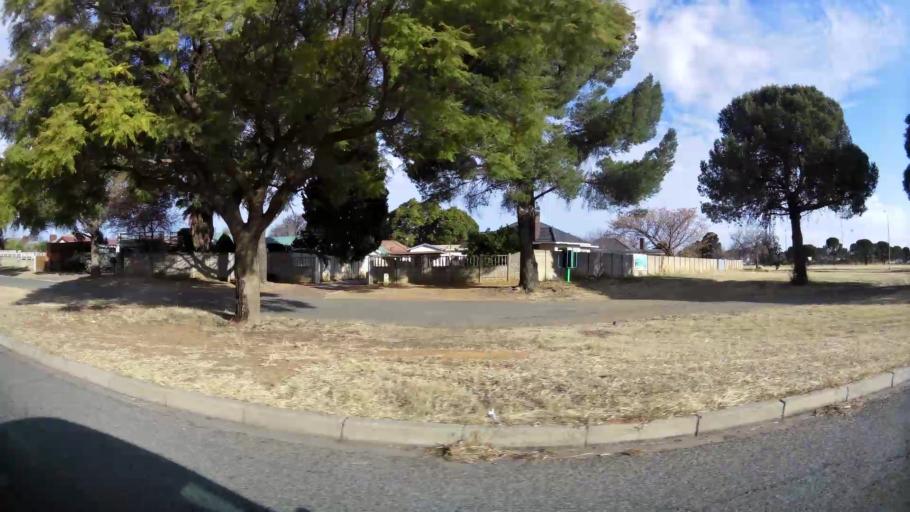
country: ZA
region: Orange Free State
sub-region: Lejweleputswa District Municipality
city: Welkom
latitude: -27.9741
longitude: 26.6968
